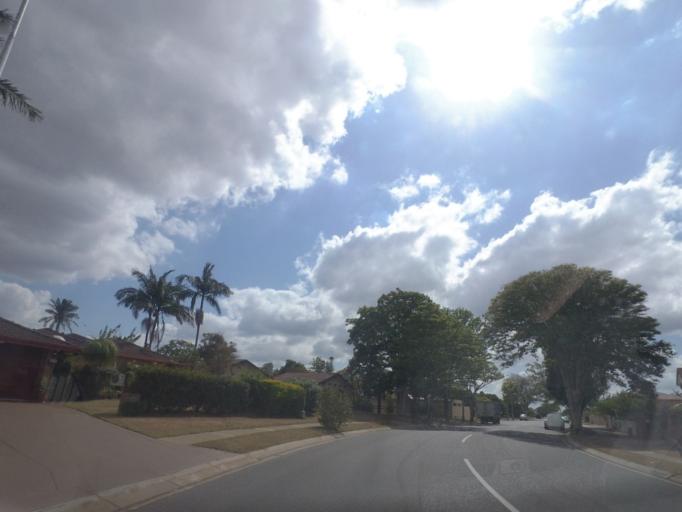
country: AU
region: Queensland
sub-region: Brisbane
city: Robertson
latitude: -27.5681
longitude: 153.0661
